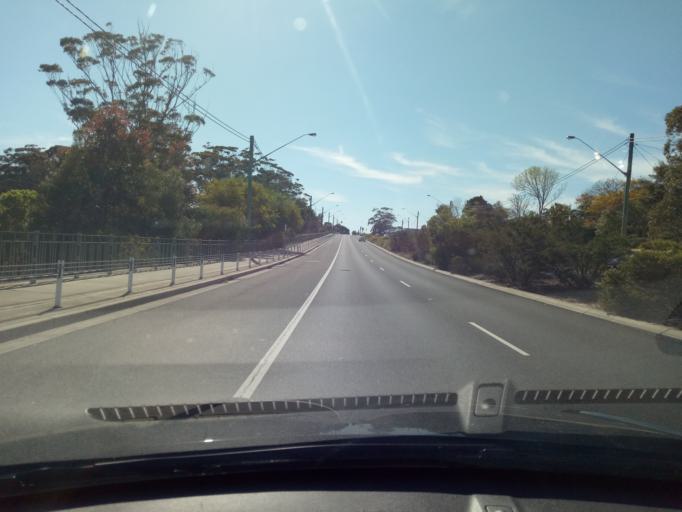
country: AU
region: New South Wales
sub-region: Gosford Shire
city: Holgate
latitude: -33.4235
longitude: 151.4350
